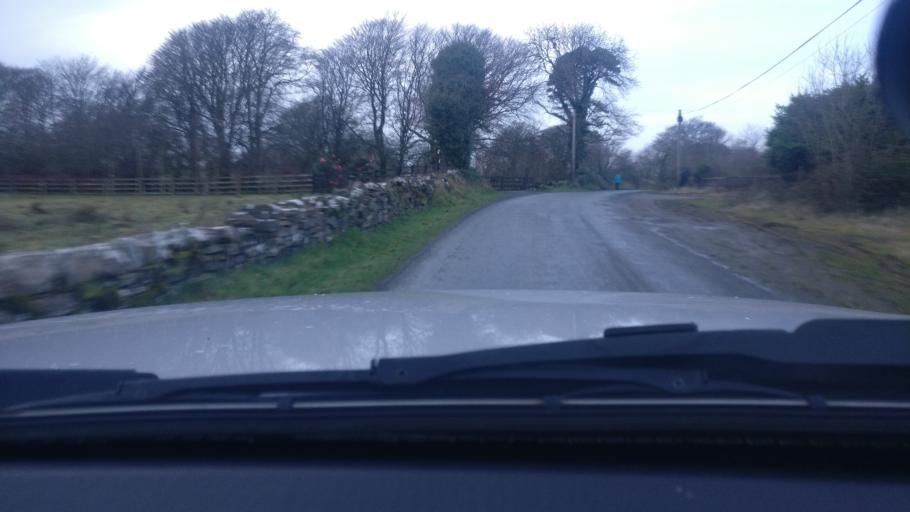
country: IE
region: Connaught
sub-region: County Galway
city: Loughrea
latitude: 53.1642
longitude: -8.5770
